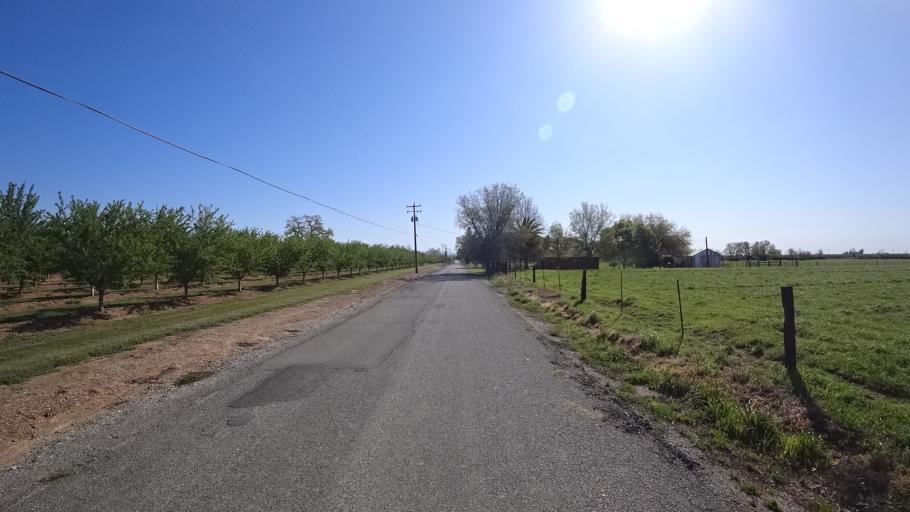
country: US
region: California
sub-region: Glenn County
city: Hamilton City
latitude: 39.7824
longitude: -122.0579
